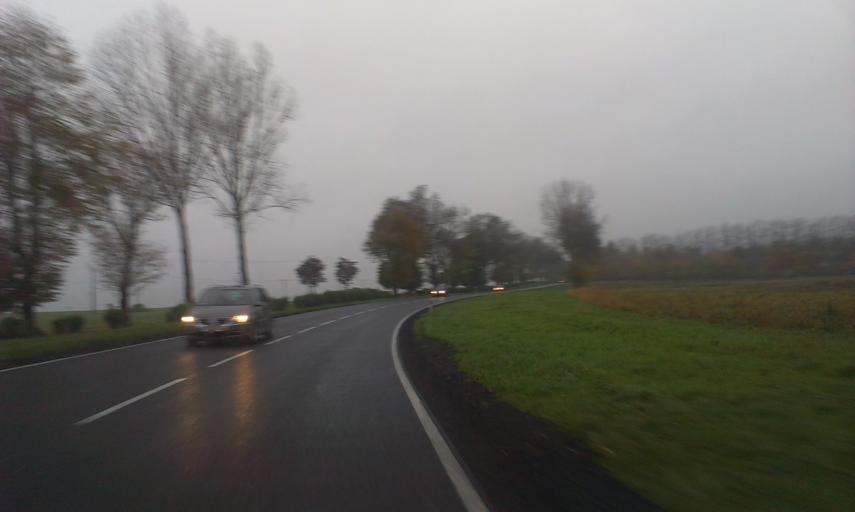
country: PL
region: West Pomeranian Voivodeship
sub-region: Powiat koszalinski
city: Sianow
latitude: 54.1448
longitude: 16.2509
